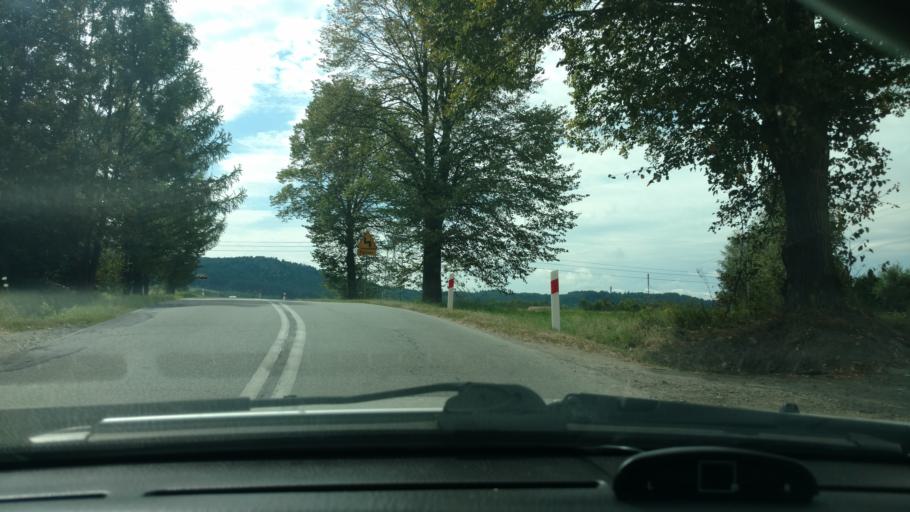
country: PL
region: Subcarpathian Voivodeship
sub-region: Powiat strzyzowski
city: Jawornik
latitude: 49.8042
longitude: 21.8702
